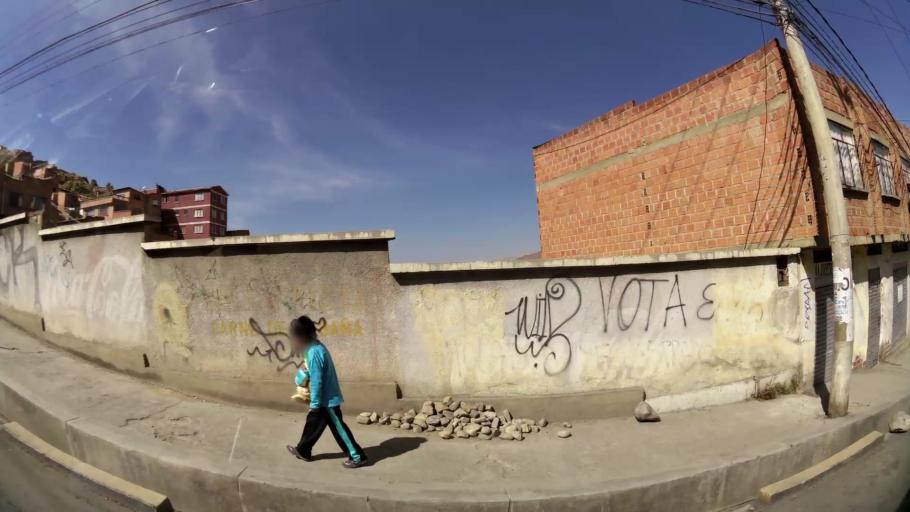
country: BO
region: La Paz
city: La Paz
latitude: -16.5265
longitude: -68.0951
